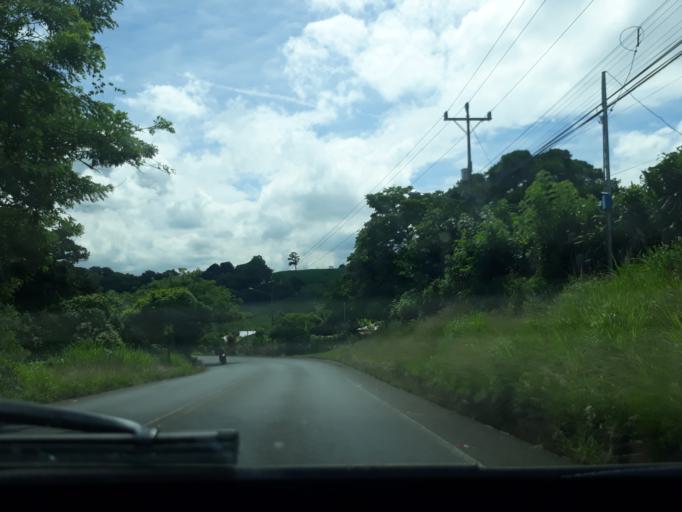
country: CR
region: Alajuela
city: Atenas
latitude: 10.0361
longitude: -84.3516
